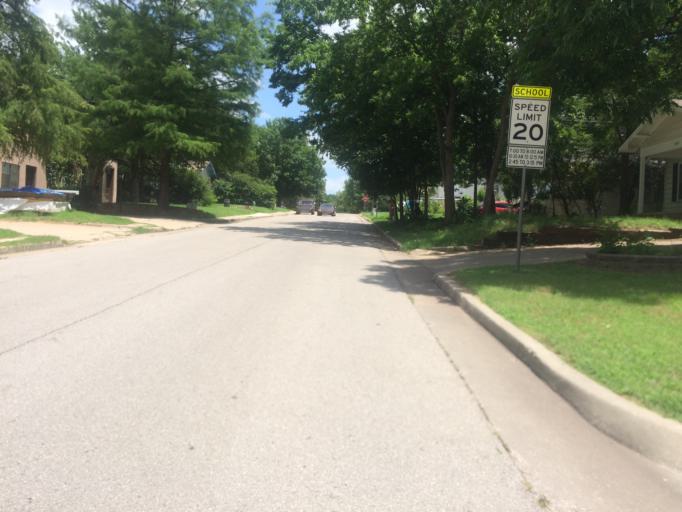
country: US
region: Oklahoma
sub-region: Cleveland County
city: Norman
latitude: 35.2075
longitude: -97.4558
